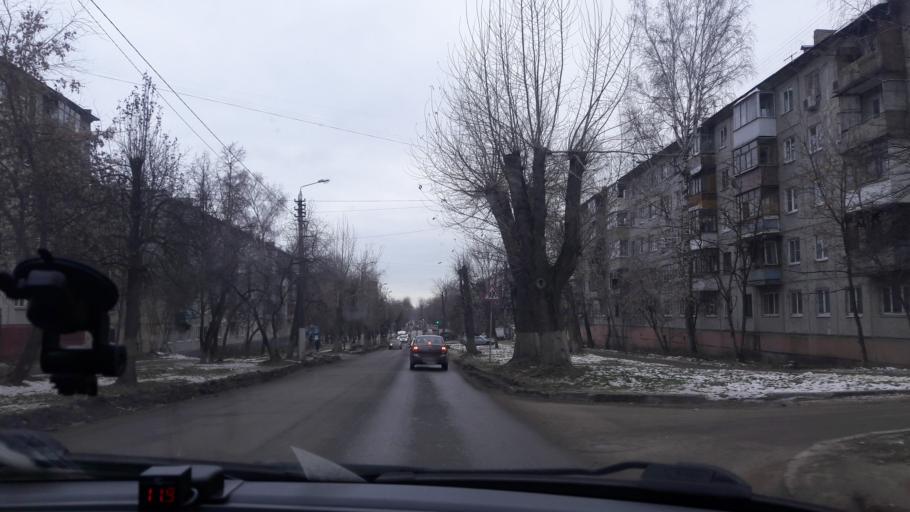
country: RU
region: Tula
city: Tula
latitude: 54.2021
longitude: 37.6577
